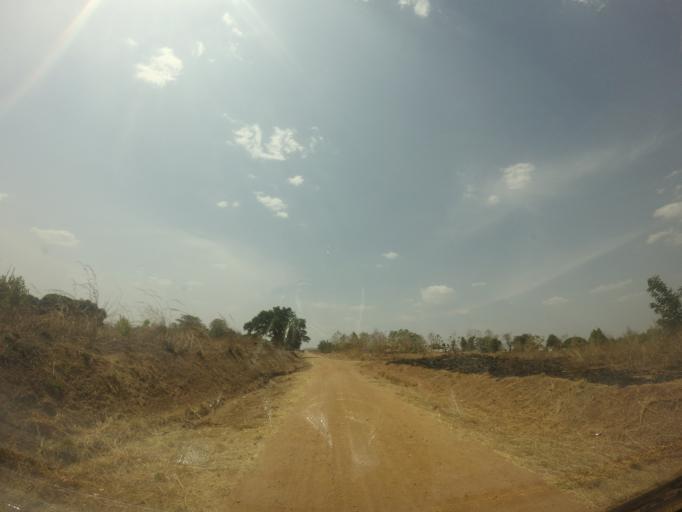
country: UG
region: Northern Region
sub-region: Arua District
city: Arua
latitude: 2.9070
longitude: 31.0658
